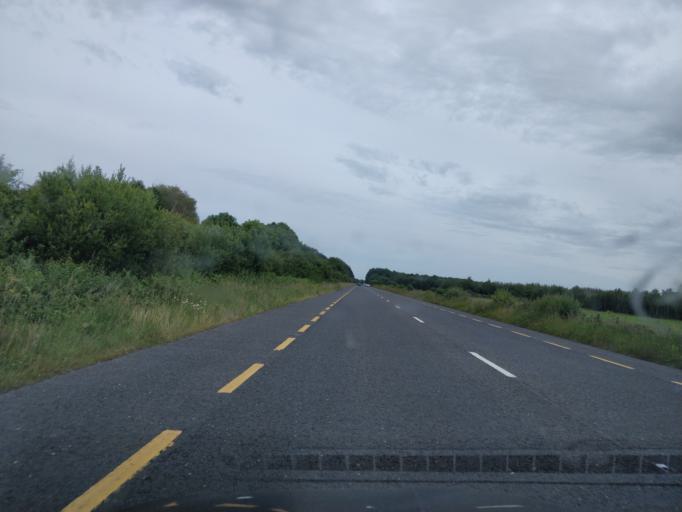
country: IE
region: Leinster
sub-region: Uibh Fhaili
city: Ferbane
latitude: 53.1617
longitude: -7.8074
